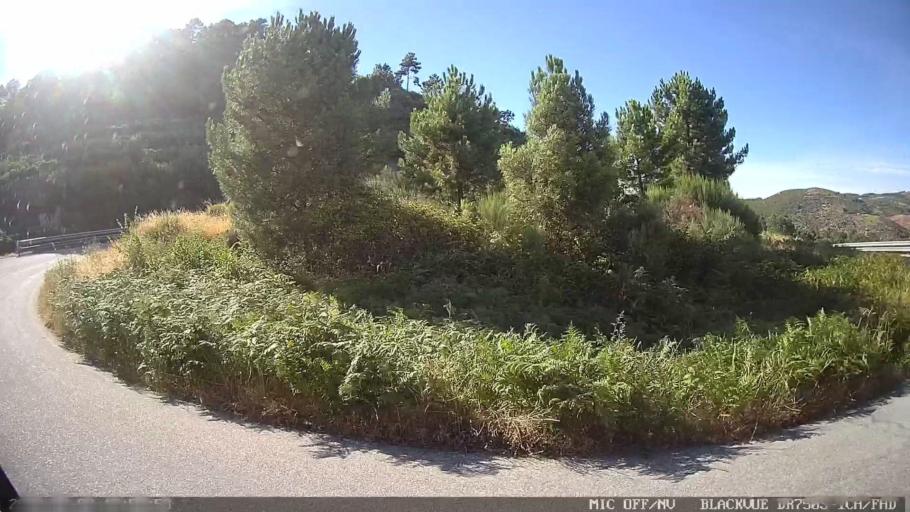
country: PT
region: Vila Real
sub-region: Murca
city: Murca
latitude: 41.4019
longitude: -7.4710
